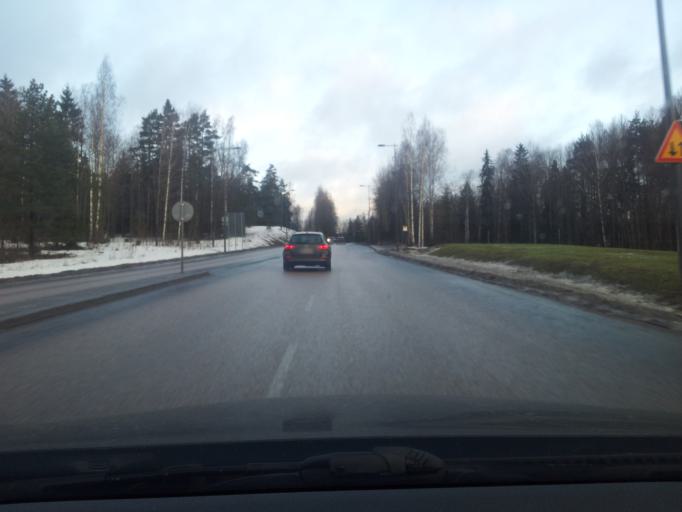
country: FI
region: Uusimaa
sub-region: Helsinki
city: Espoo
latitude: 60.1610
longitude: 24.6265
